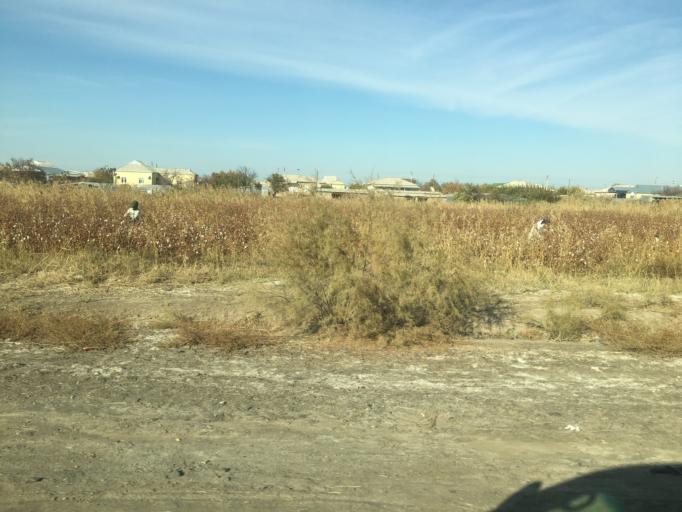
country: TM
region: Mary
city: Mary
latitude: 37.6064
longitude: 61.7298
